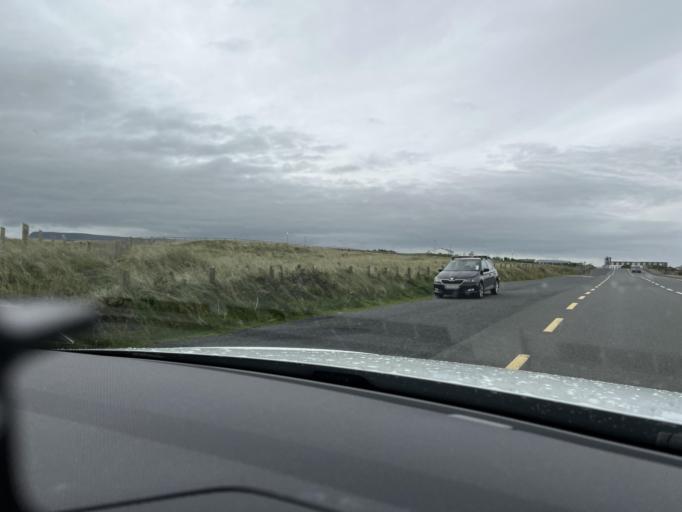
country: IE
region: Connaught
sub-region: Sligo
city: Strandhill
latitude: 54.3067
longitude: -8.5729
